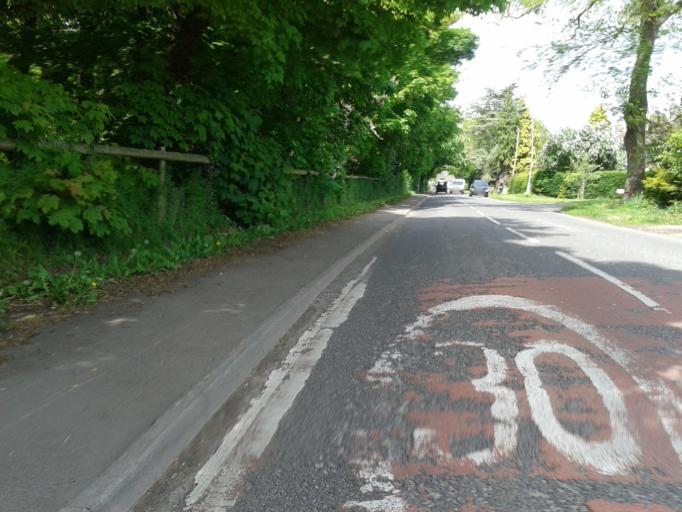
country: GB
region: England
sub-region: Cambridgeshire
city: Meldreth
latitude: 52.1108
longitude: 0.0367
